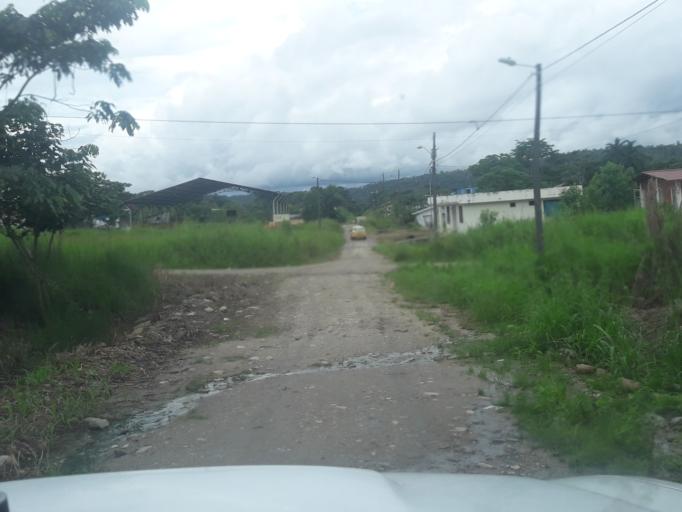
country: EC
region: Napo
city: Archidona
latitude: -0.9479
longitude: -77.8167
